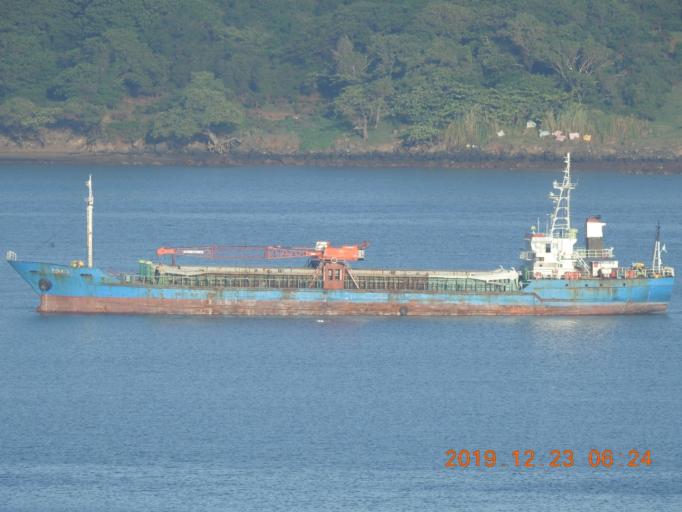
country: MG
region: Diana
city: Antsiranana
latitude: -12.2689
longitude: 49.2920
